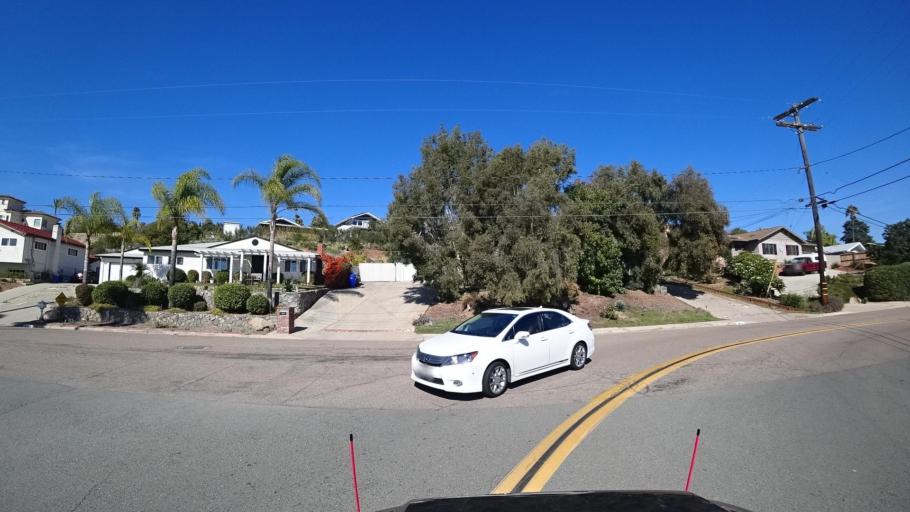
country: US
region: California
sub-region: San Diego County
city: Casa de Oro-Mount Helix
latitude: 32.7581
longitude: -116.9790
